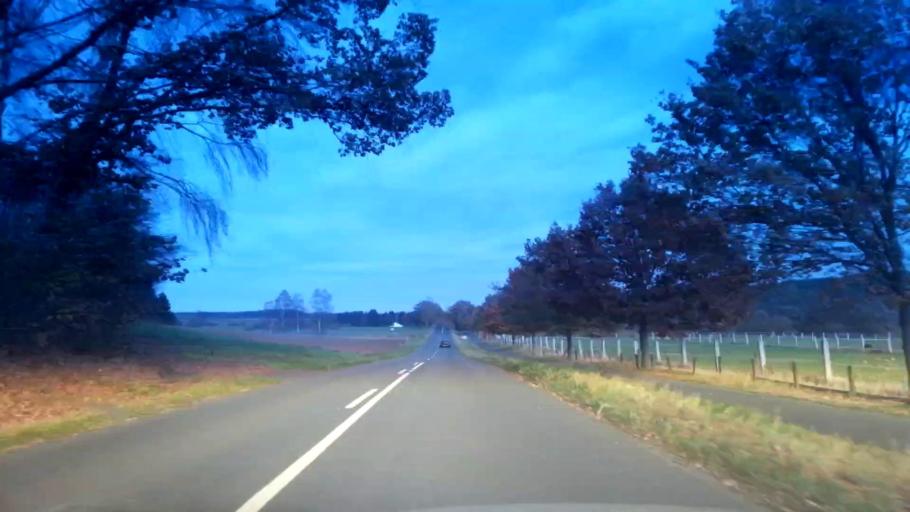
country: DE
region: Bavaria
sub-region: Upper Palatinate
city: Waldsassen
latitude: 50.0146
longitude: 12.3190
